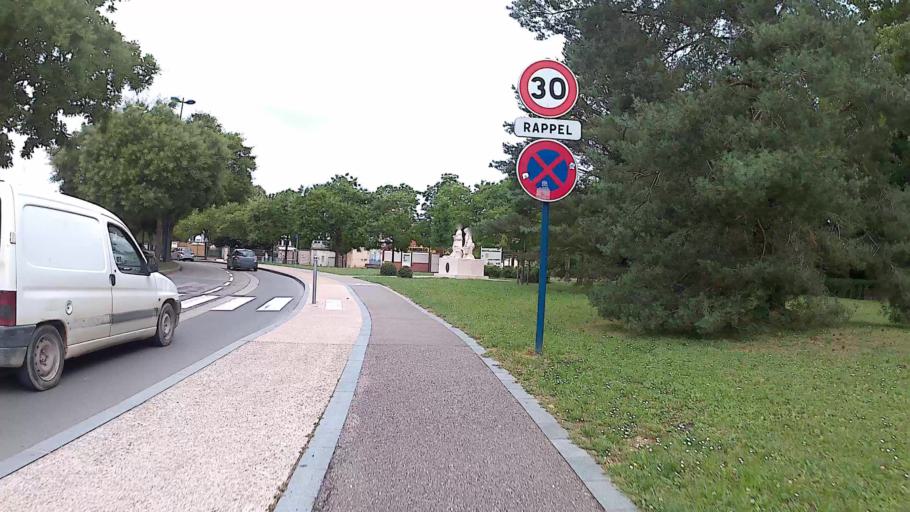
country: FR
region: Lorraine
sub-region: Departement de la Meuse
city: Verdun
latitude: 49.1638
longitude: 5.3863
